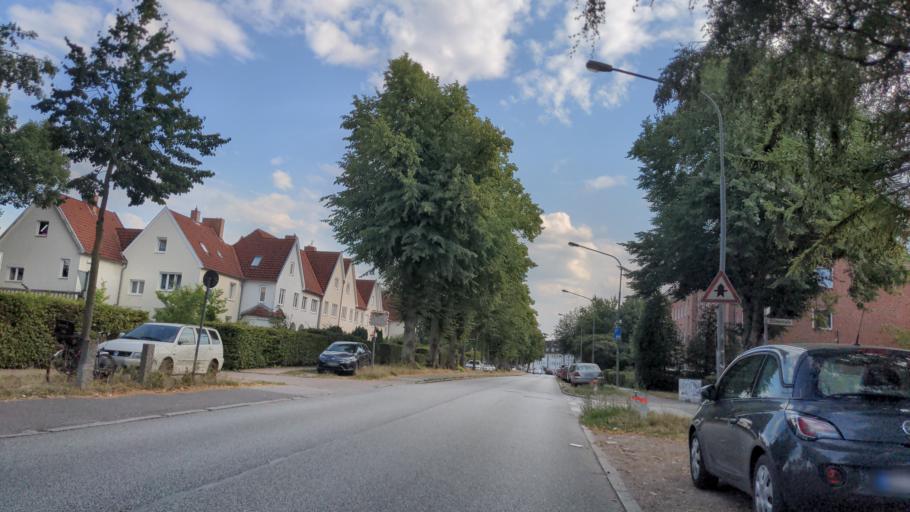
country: DE
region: Schleswig-Holstein
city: Luebeck
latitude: 53.8708
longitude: 10.7204
